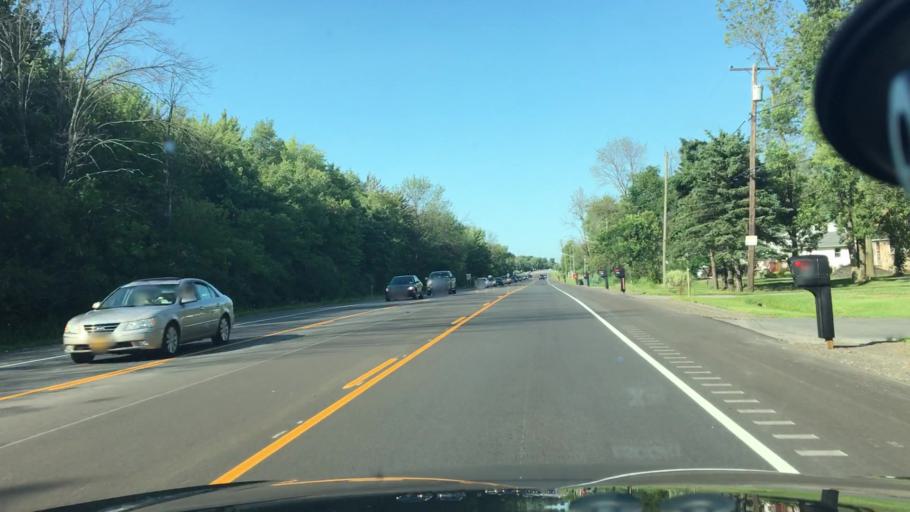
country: US
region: New York
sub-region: Erie County
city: Wanakah
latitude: 42.7311
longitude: -78.8851
